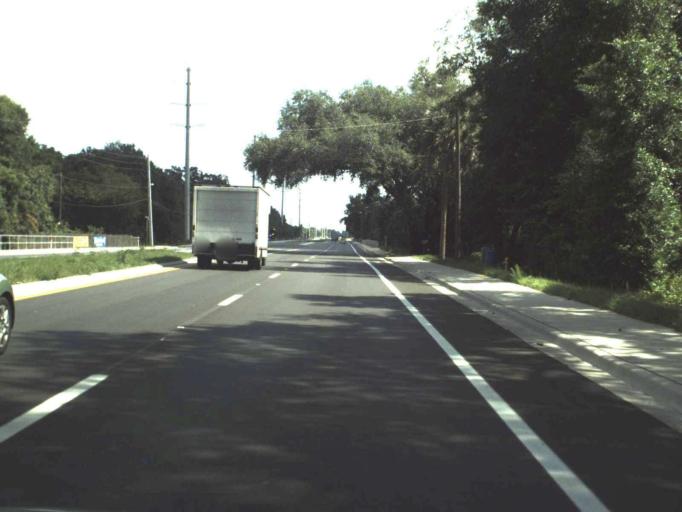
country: US
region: Florida
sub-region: Seminole County
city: Midway
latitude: 28.8558
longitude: -81.1621
